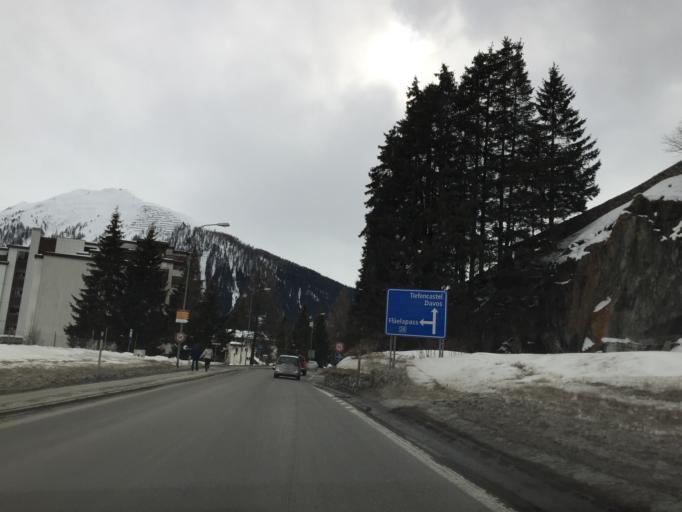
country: CH
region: Grisons
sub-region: Praettigau/Davos District
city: Davos
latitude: 46.8134
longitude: 9.8455
